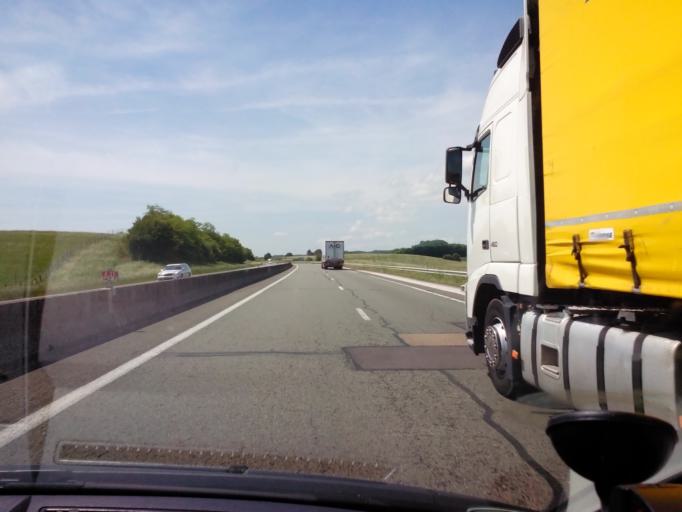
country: FR
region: Champagne-Ardenne
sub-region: Departement de la Haute-Marne
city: Avrecourt
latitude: 48.0167
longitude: 5.5254
